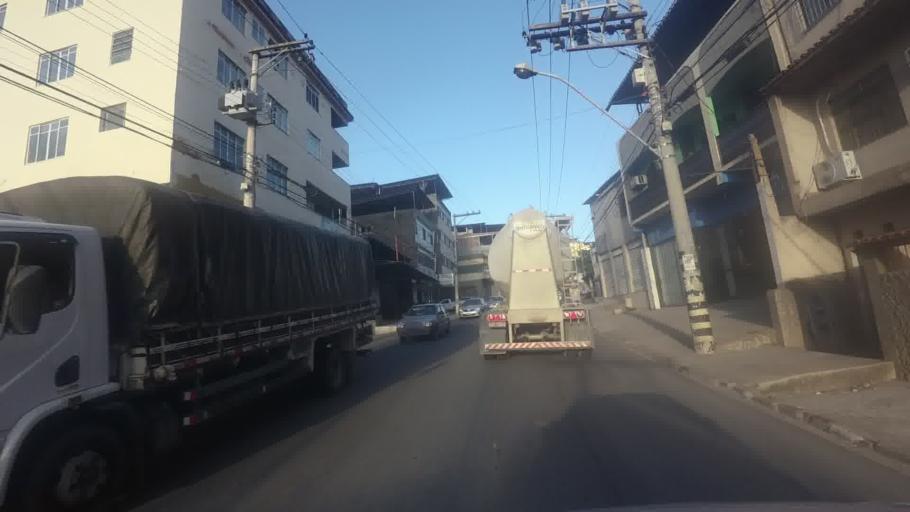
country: BR
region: Espirito Santo
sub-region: Cachoeiro De Itapemirim
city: Cachoeiro de Itapemirim
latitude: -20.8480
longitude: -41.1461
